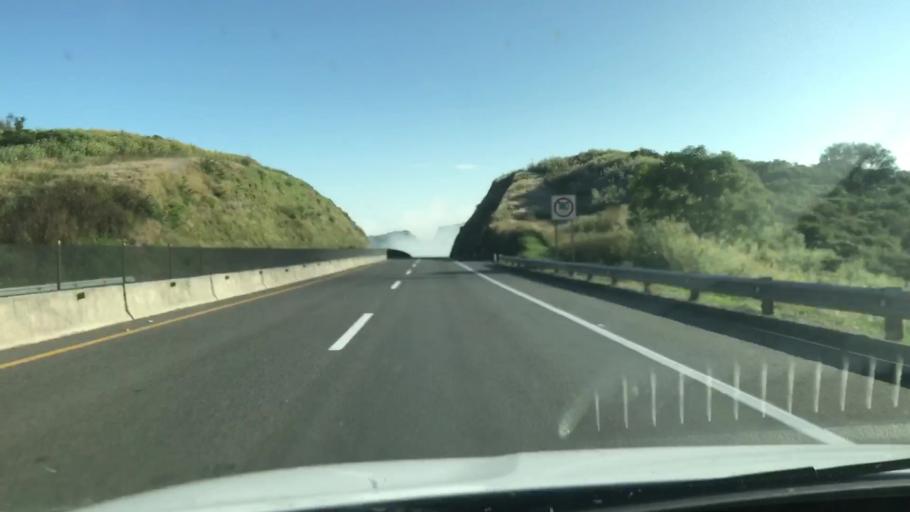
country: MX
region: Jalisco
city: Jalostotitlan
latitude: 21.1284
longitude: -102.4469
